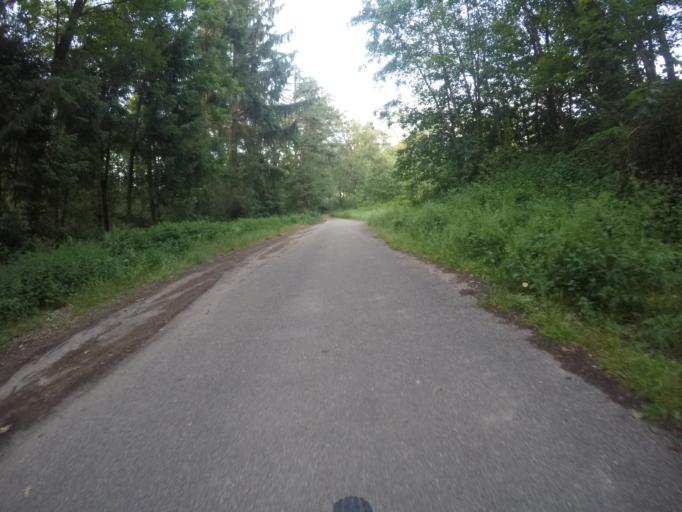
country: DE
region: North Rhine-Westphalia
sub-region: Regierungsbezirk Munster
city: Isselburg
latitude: 51.8242
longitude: 6.4350
